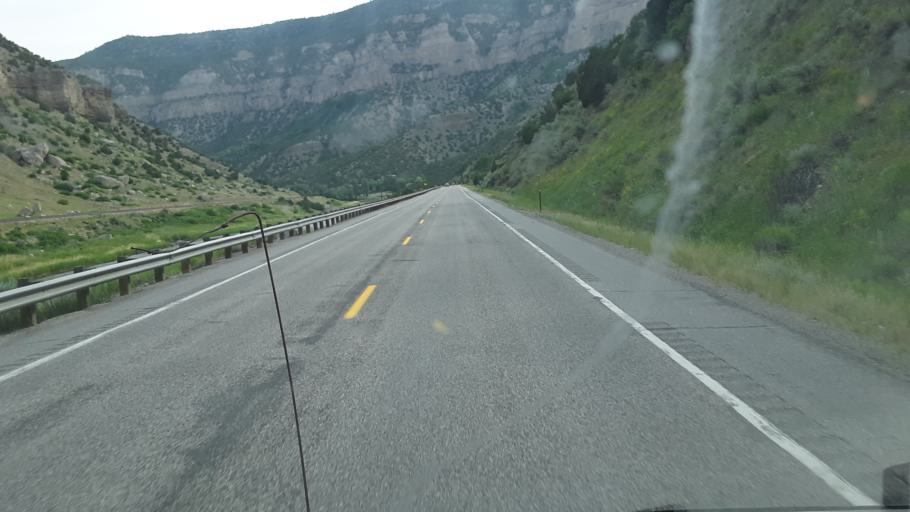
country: US
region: Wyoming
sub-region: Hot Springs County
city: Thermopolis
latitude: 43.4851
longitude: -108.1653
